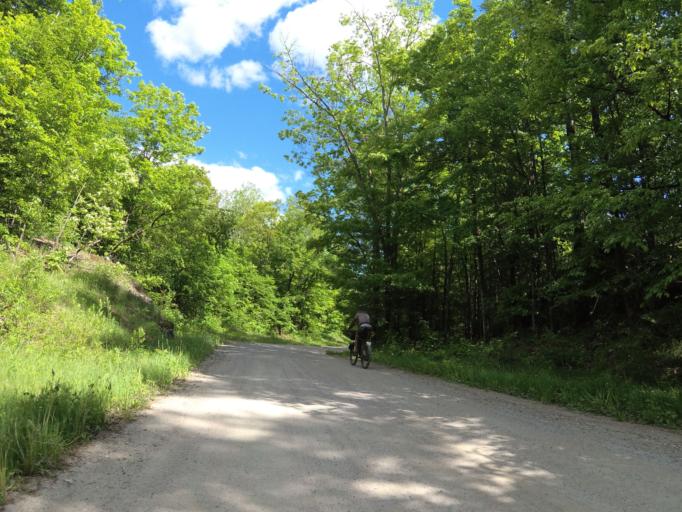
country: CA
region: Ontario
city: Renfrew
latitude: 45.0414
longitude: -76.8193
